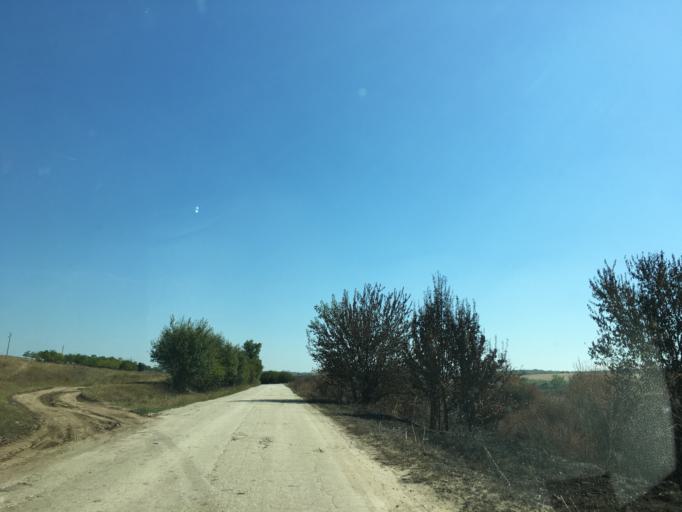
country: BG
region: Pleven
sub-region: Obshtina Knezha
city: Knezha
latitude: 43.5383
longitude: 24.1128
